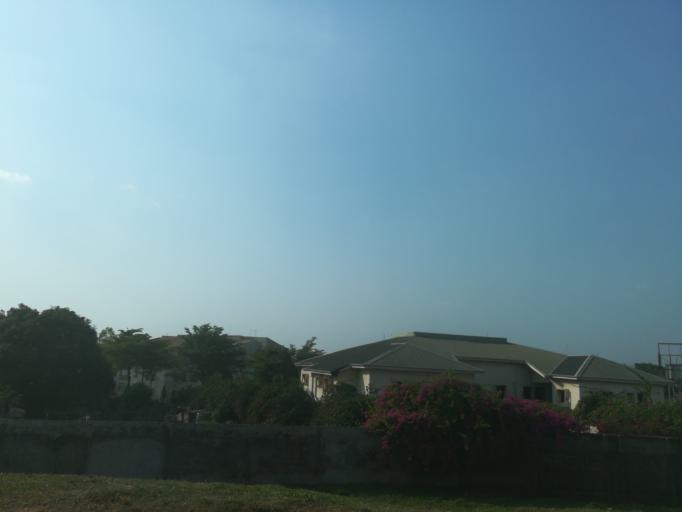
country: NG
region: Abuja Federal Capital Territory
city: Abuja
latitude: 9.0758
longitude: 7.4540
